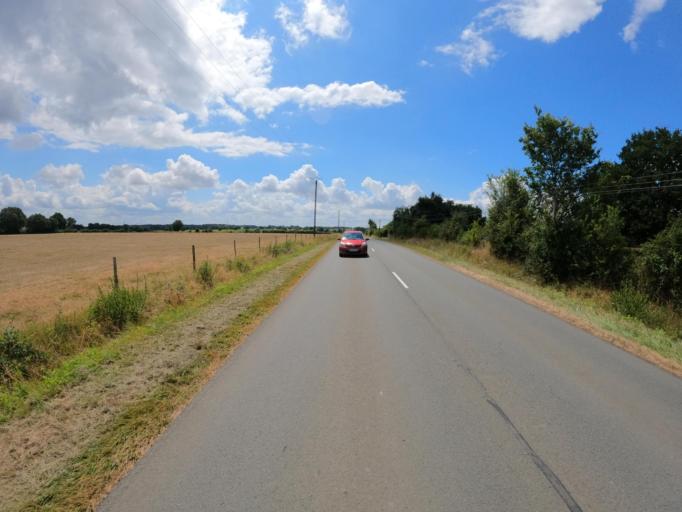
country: FR
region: Pays de la Loire
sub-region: Departement de Maine-et-Loire
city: Chateauneuf-sur-Sarthe
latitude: 47.7133
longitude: -0.5315
